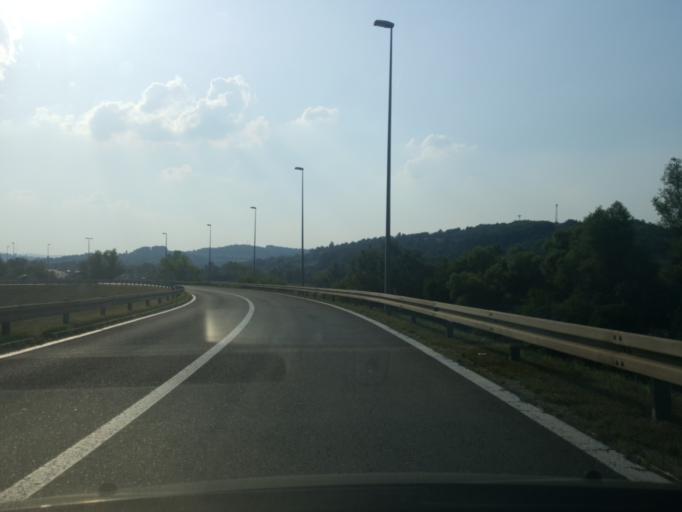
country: RS
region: Central Serbia
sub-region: Belgrade
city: Sopot
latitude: 44.5666
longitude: 20.6673
